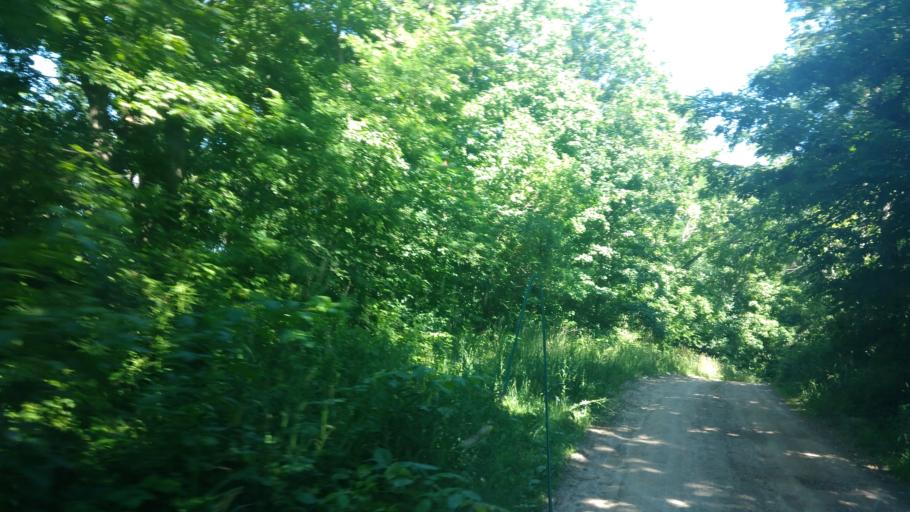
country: US
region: New York
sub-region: Wayne County
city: Clyde
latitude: 43.0251
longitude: -76.8723
